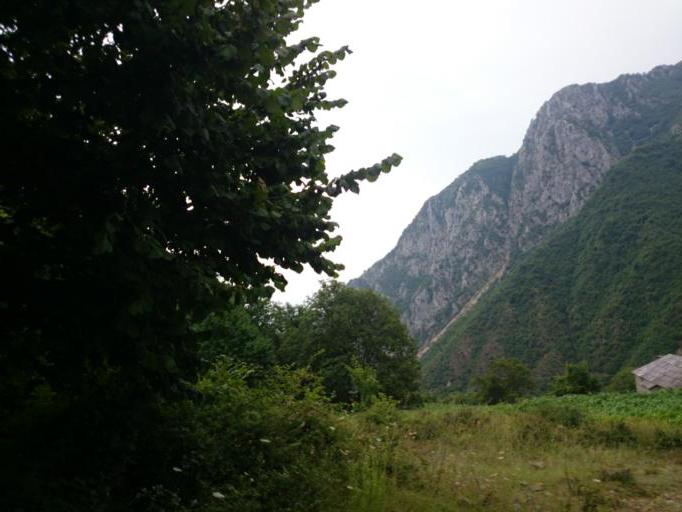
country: AL
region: Diber
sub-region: Rrethi i Dibres
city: Fushe-Lure
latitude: 41.7610
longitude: 20.2245
